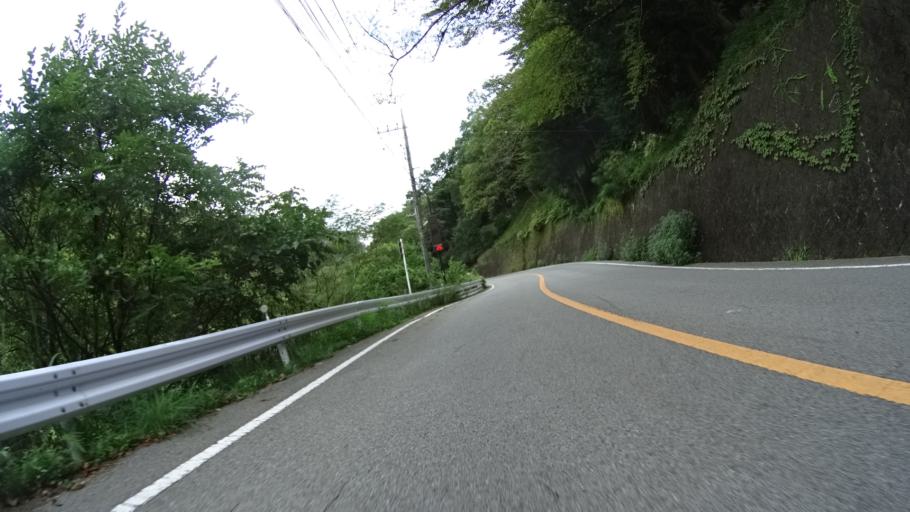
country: JP
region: Yamanashi
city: Kofu-shi
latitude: 35.7020
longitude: 138.5589
